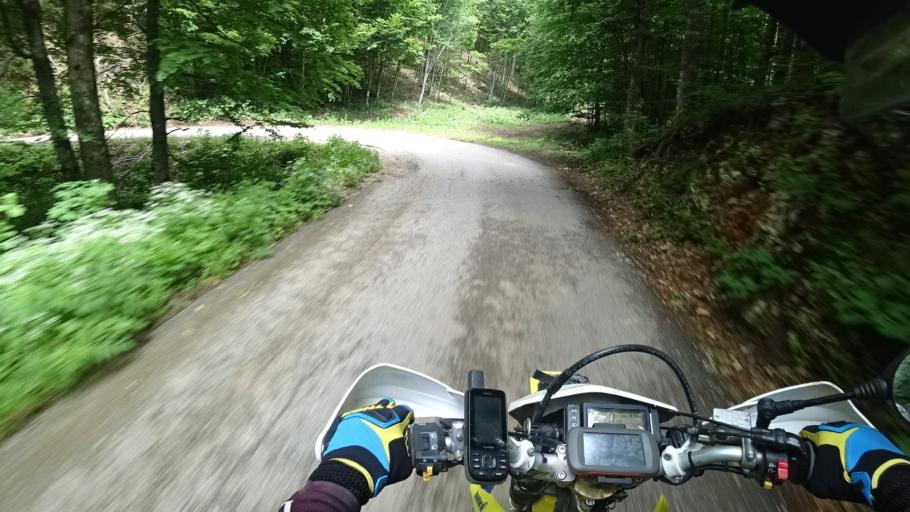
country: HR
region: Primorsko-Goranska
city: Bribir
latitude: 45.2514
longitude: 14.7894
